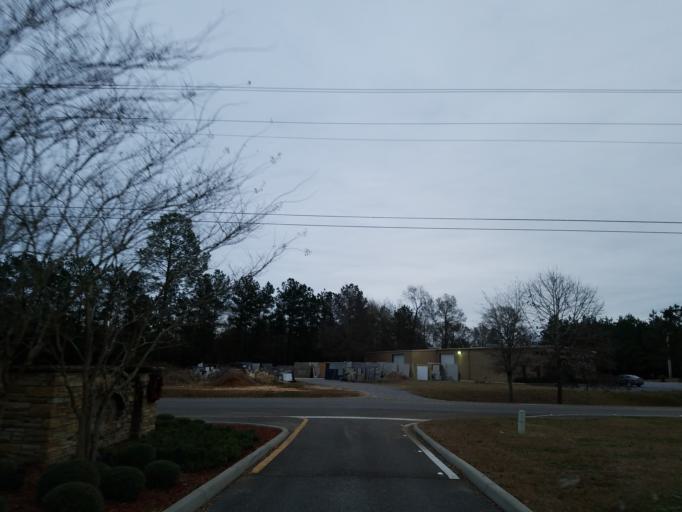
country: US
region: Mississippi
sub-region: Jones County
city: Ellisville
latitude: 31.5513
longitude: -89.2526
